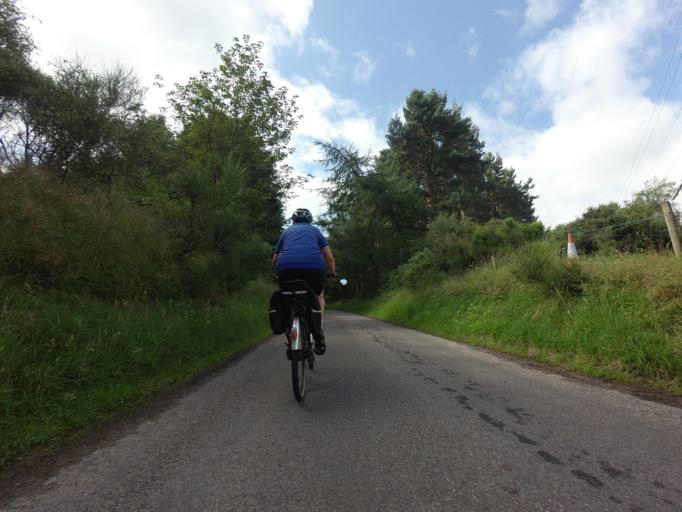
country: GB
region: Scotland
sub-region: Highland
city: Nairn
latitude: 57.5679
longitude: -3.8661
